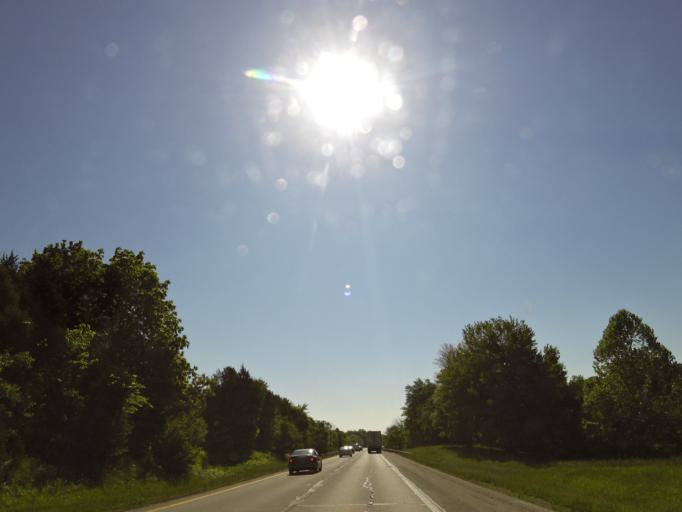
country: US
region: Kentucky
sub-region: Franklin County
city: Frankfort
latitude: 38.1500
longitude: -85.0501
